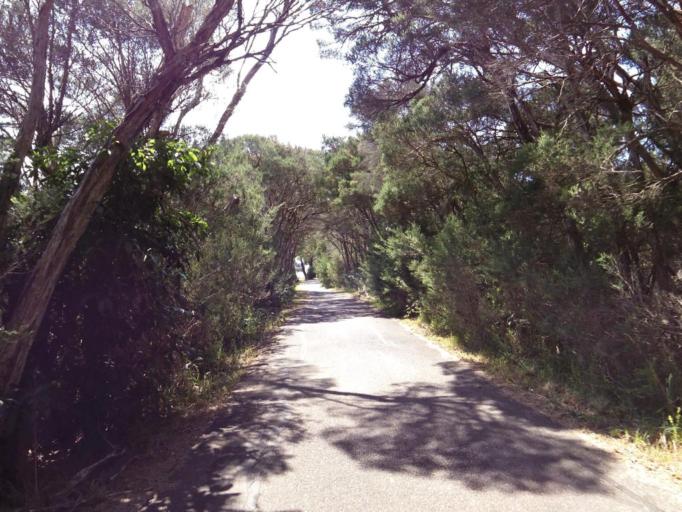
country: AU
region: Victoria
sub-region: Mornington Peninsula
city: Hastings
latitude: -38.3245
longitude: 145.1831
